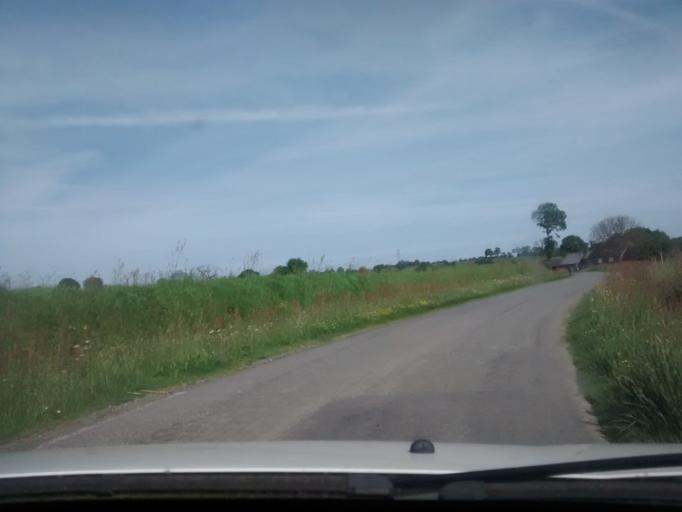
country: FR
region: Brittany
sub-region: Departement d'Ille-et-Vilaine
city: Javene
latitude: 48.3322
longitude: -1.2343
